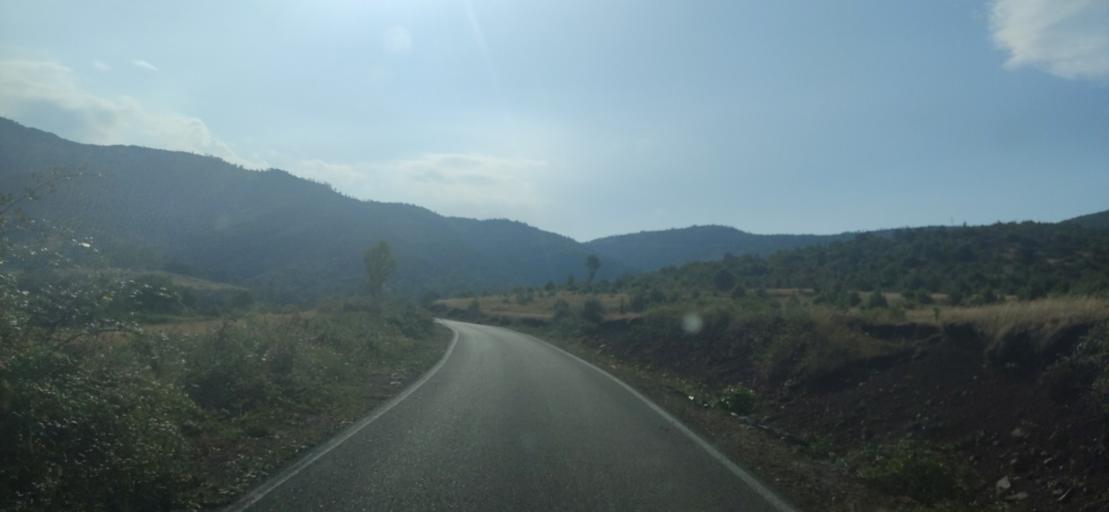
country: AL
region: Shkoder
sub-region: Rrethi i Pukes
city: Iballe
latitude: 42.1825
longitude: 19.9958
